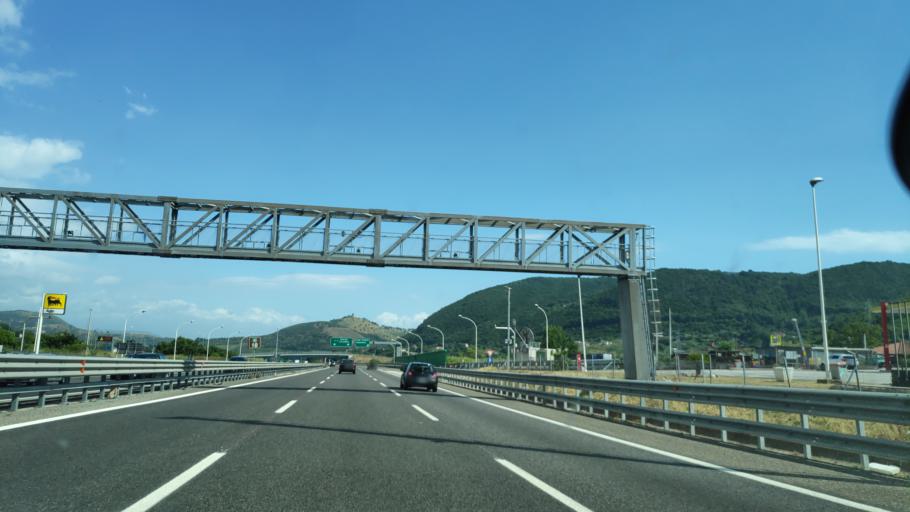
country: IT
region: Campania
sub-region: Provincia di Salerno
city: San Mango Piemonte
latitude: 40.6928
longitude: 14.8347
